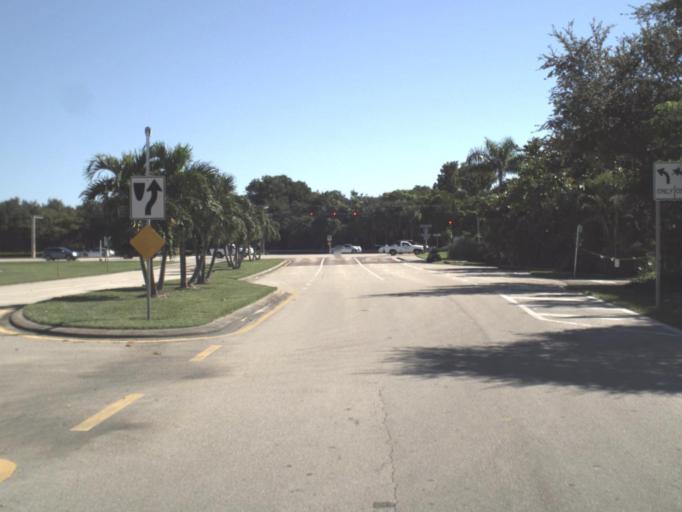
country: US
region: Florida
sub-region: Collier County
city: Naples
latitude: 26.1459
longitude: -81.7679
